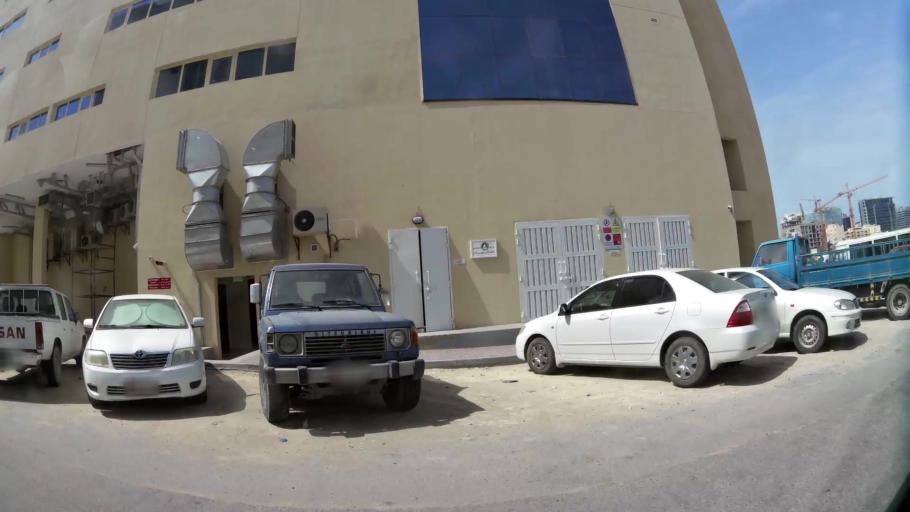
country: QA
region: Baladiyat ad Dawhah
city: Doha
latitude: 25.2816
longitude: 51.5383
